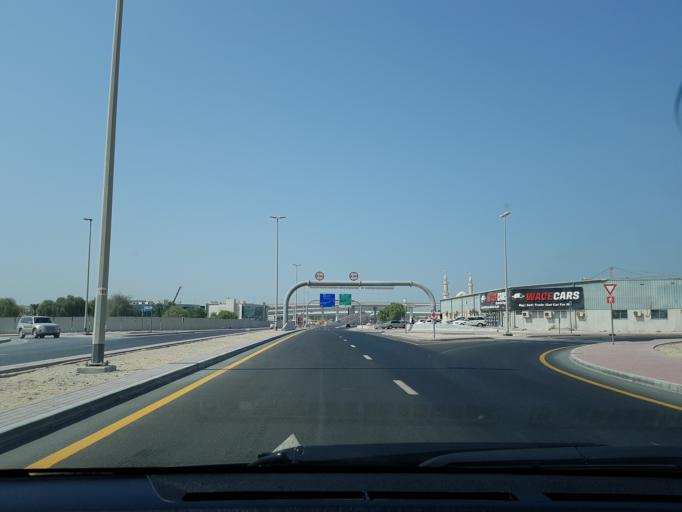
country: AE
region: Dubai
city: Dubai
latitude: 25.1615
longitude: 55.2397
